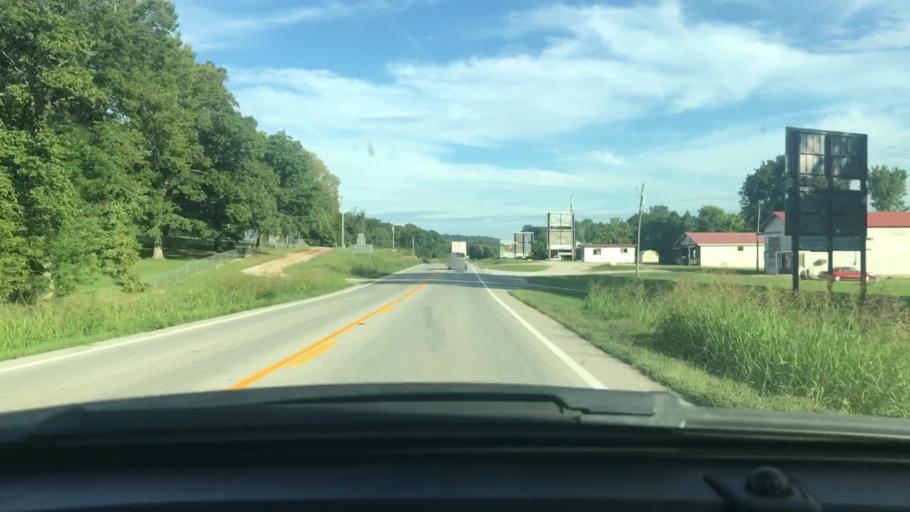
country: US
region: Arkansas
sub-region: Sharp County
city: Cherokee Village
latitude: 36.3016
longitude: -91.4437
